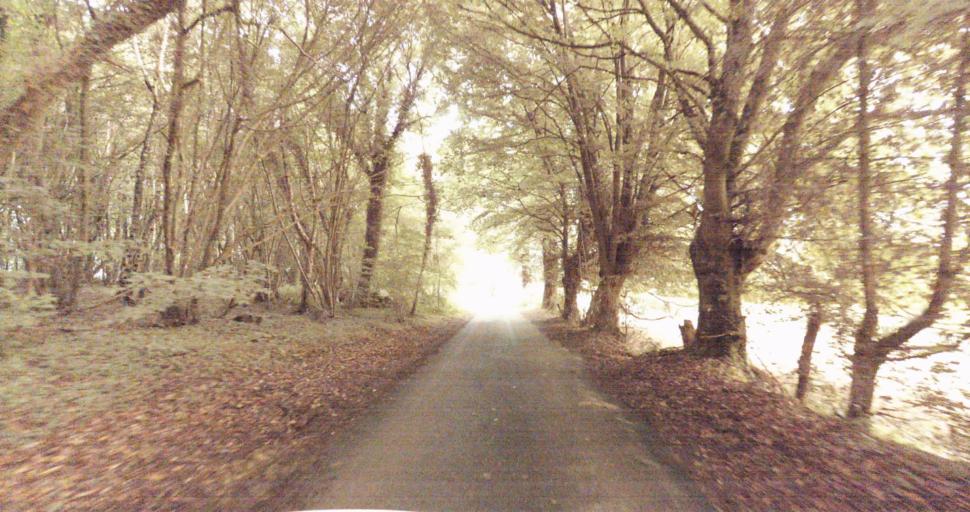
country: FR
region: Lower Normandy
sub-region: Departement de l'Orne
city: Trun
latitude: 48.8898
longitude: 0.0919
